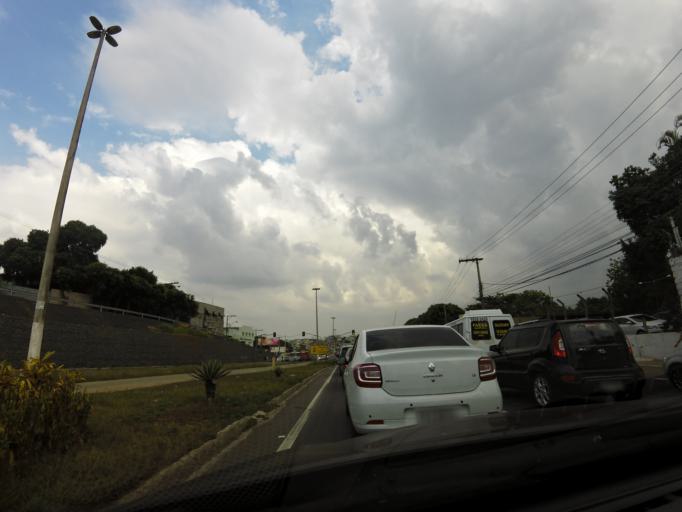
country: BR
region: Espirito Santo
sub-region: Vitoria
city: Vitoria
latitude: -20.3359
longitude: -40.3776
